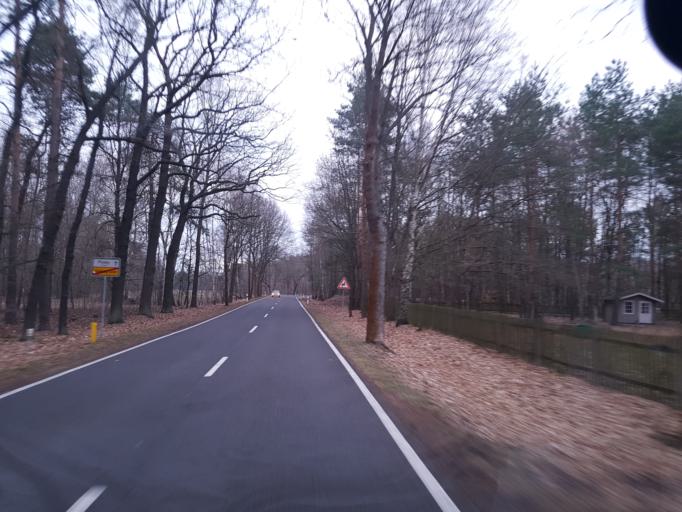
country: DE
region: Brandenburg
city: Sallgast
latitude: 51.5780
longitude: 13.8501
